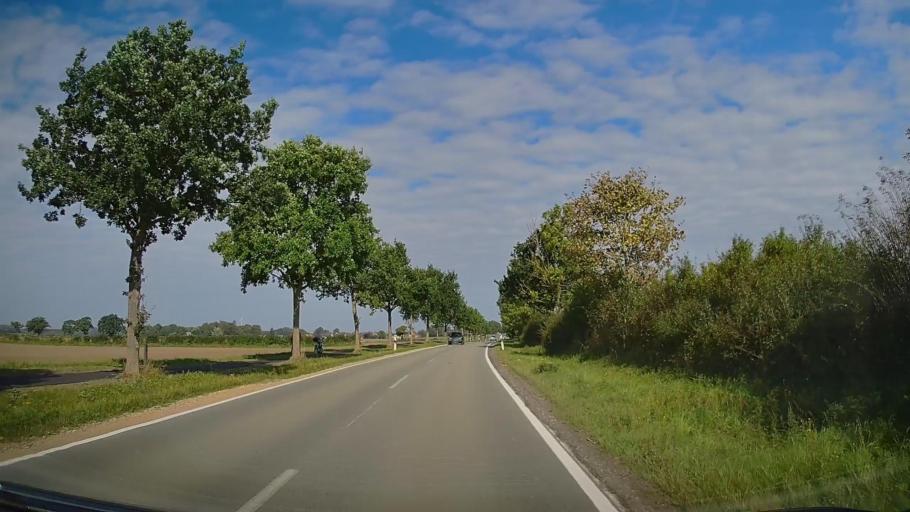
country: DE
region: Schleswig-Holstein
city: Oldenburg in Holstein
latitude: 54.3101
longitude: 10.8865
